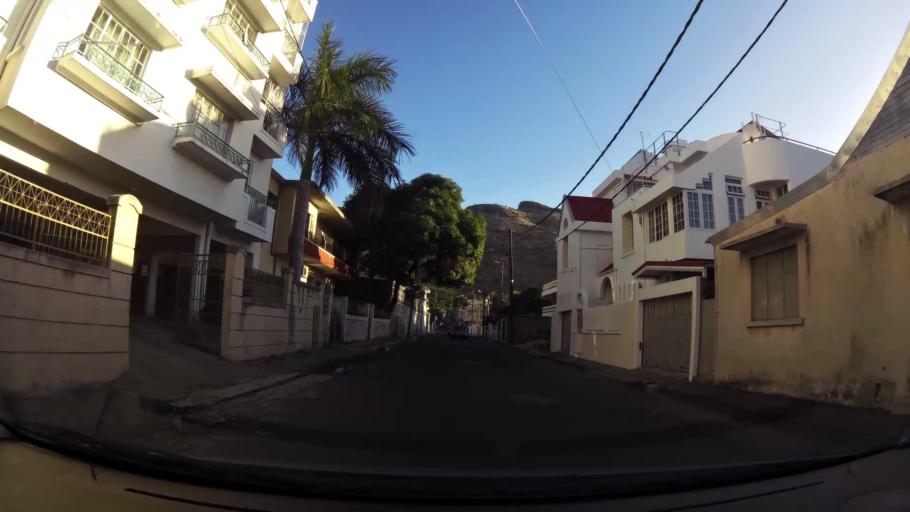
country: MU
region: Port Louis
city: Port Louis
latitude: -20.1719
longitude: 57.5057
